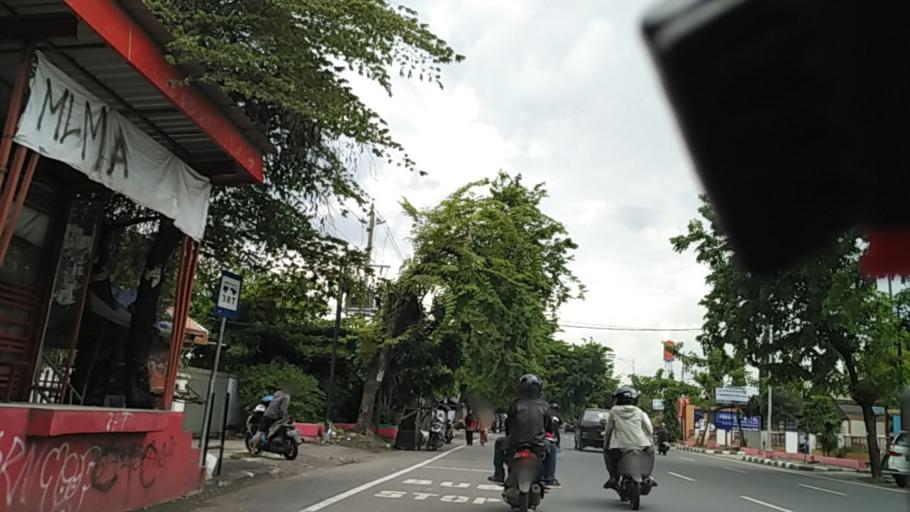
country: ID
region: Central Java
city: Semarang
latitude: -6.9899
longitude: 110.4345
